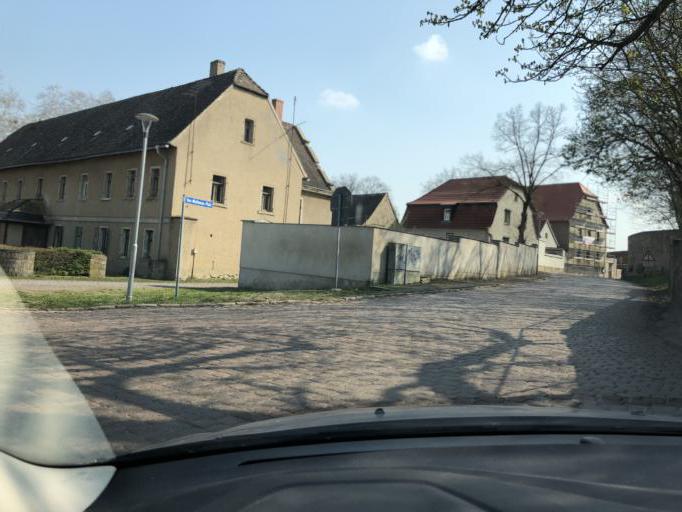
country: DE
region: Saxony-Anhalt
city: Hohenthurm
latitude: 51.5232
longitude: 12.0967
